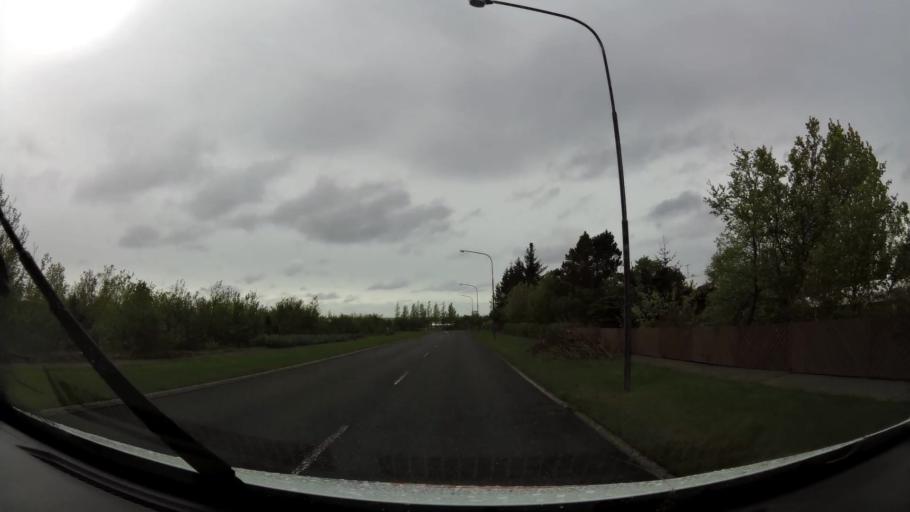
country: IS
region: Capital Region
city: Gardabaer
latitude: 64.1013
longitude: -21.9226
